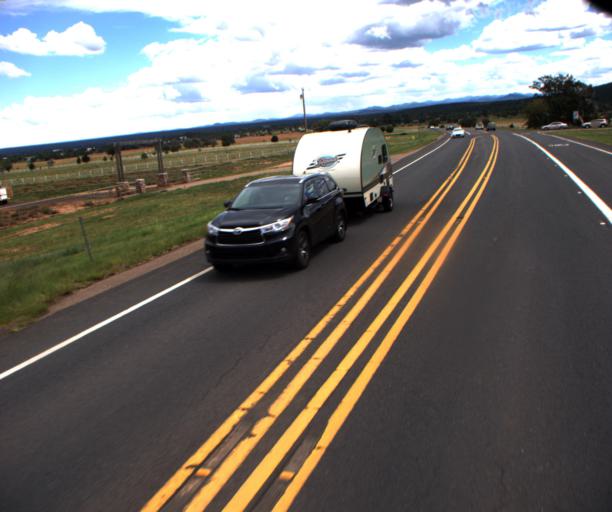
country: US
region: Arizona
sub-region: Navajo County
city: Linden
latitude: 34.2864
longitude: -110.1701
